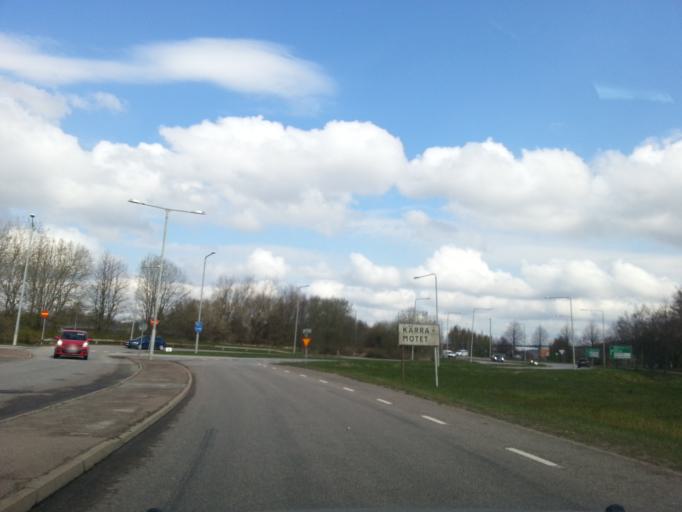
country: SE
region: Vaestra Goetaland
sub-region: Goteborg
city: Gardsten
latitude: 57.7857
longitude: 12.0021
